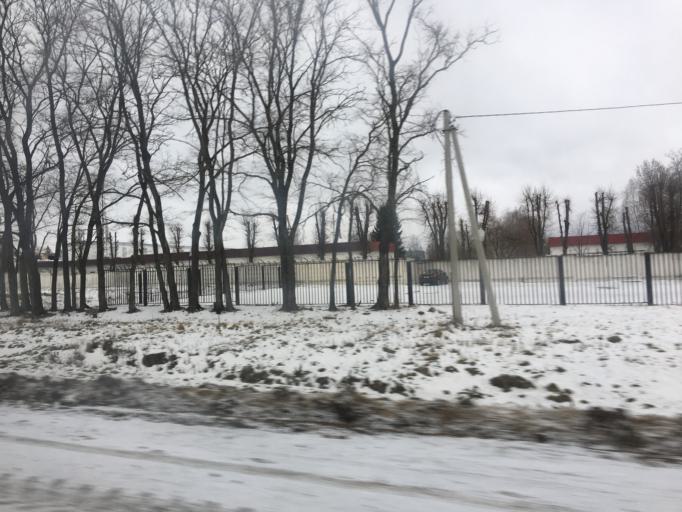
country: RU
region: Tula
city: Pervomayskiy
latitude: 54.0396
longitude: 37.5260
